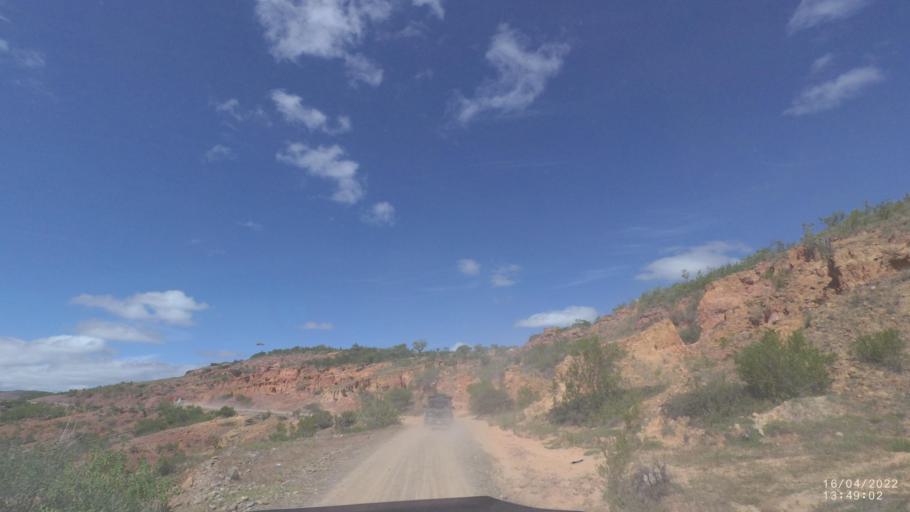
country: BO
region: Cochabamba
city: Mizque
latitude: -18.0133
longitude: -65.5795
